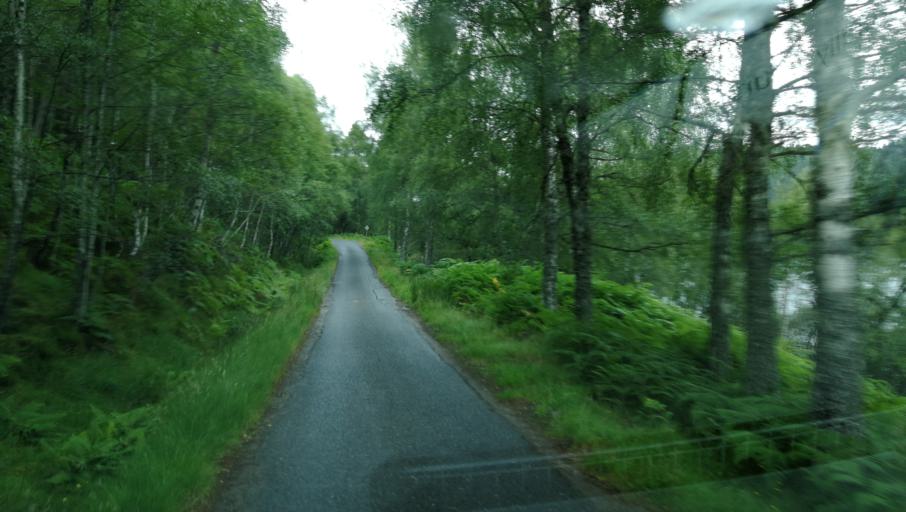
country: GB
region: Scotland
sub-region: Highland
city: Spean Bridge
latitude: 57.2837
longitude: -4.9257
